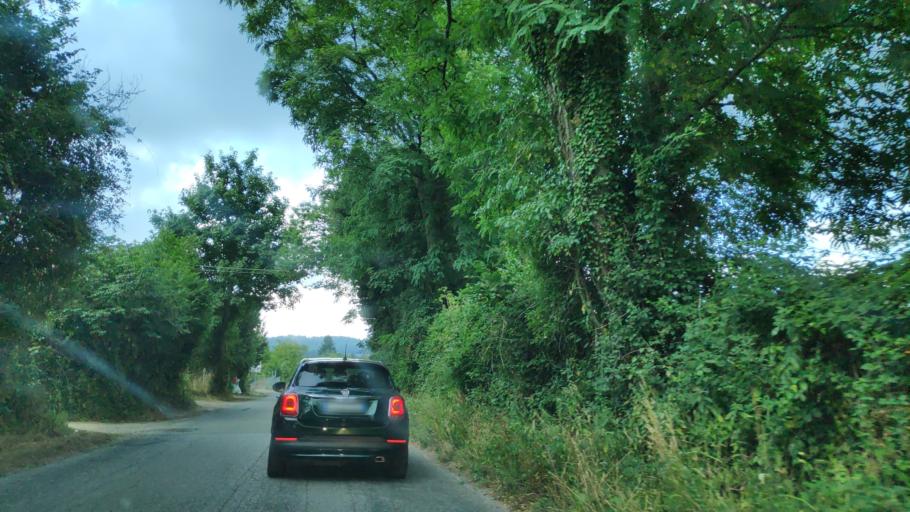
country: IT
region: Calabria
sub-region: Provincia di Vibo-Valentia
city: Serra San Bruno
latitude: 38.5612
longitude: 16.3261
